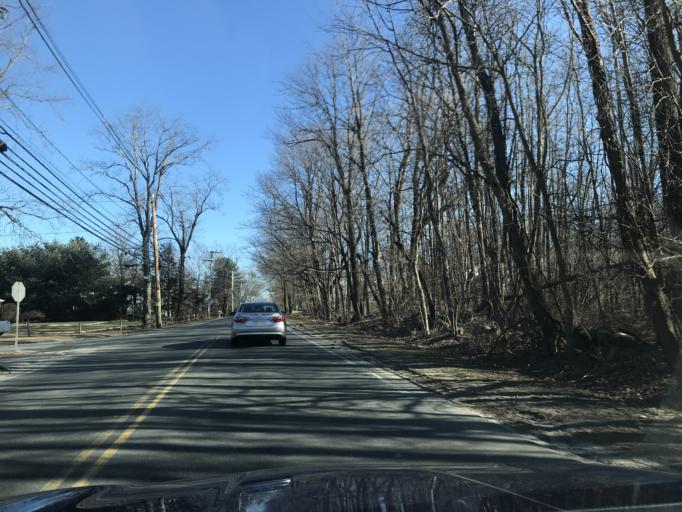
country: US
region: Massachusetts
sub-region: Essex County
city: Groveland
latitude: 42.7203
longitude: -71.0069
